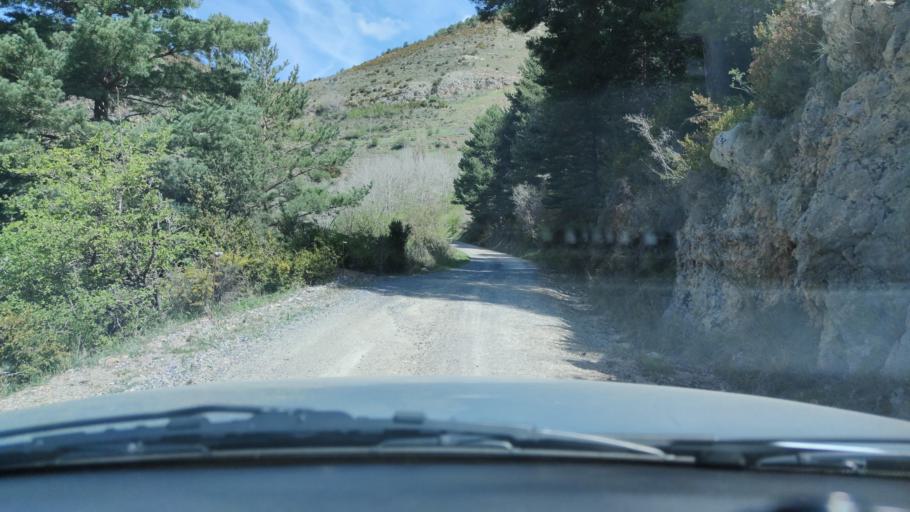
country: ES
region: Catalonia
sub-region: Provincia de Lleida
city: Sort
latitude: 42.2941
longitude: 1.1819
